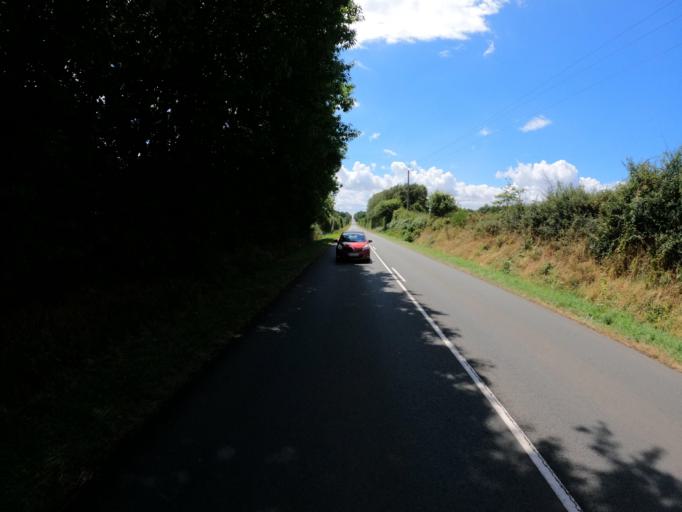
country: FR
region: Pays de la Loire
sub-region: Departement de Maine-et-Loire
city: Champigne
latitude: 47.6934
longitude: -0.5483
